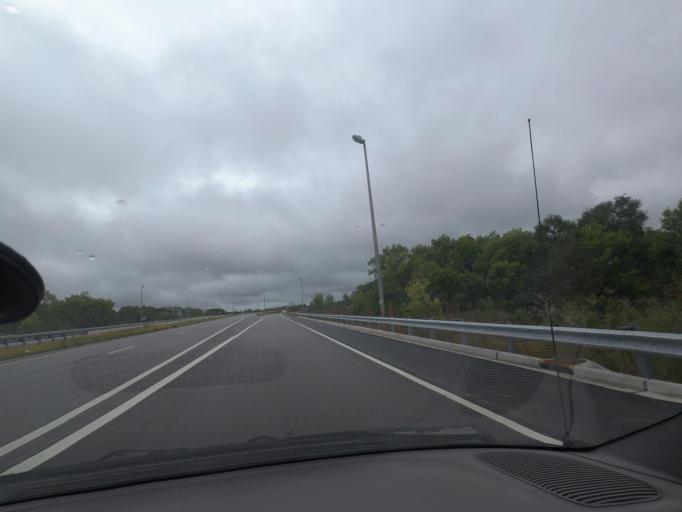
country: US
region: Illinois
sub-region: Macon County
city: Harristown
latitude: 39.8419
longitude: -89.0397
